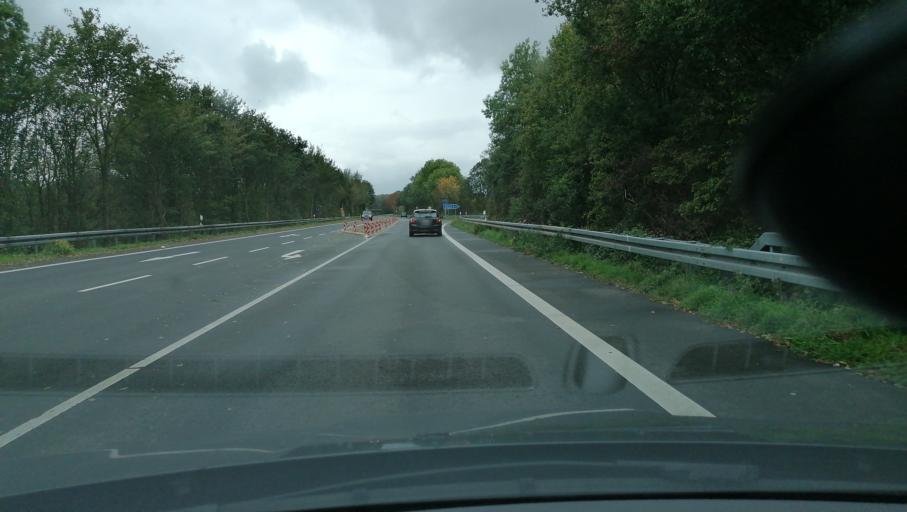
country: DE
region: North Rhine-Westphalia
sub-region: Regierungsbezirk Munster
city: Recklinghausen
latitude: 51.6536
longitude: 7.1674
